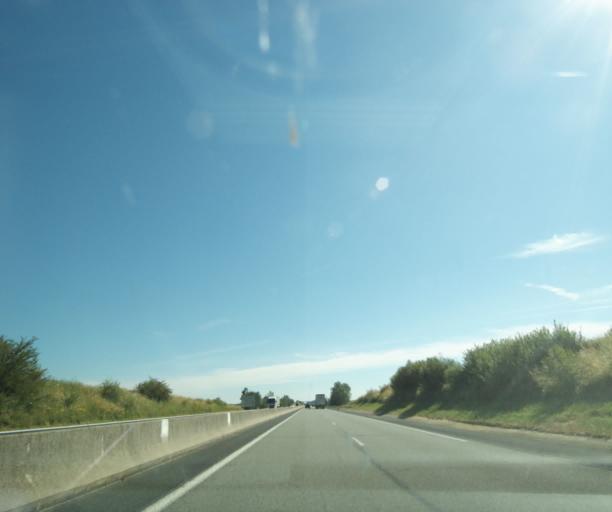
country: FR
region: Lorraine
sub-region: Departement des Vosges
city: Lamarche
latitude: 48.1644
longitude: 5.7081
